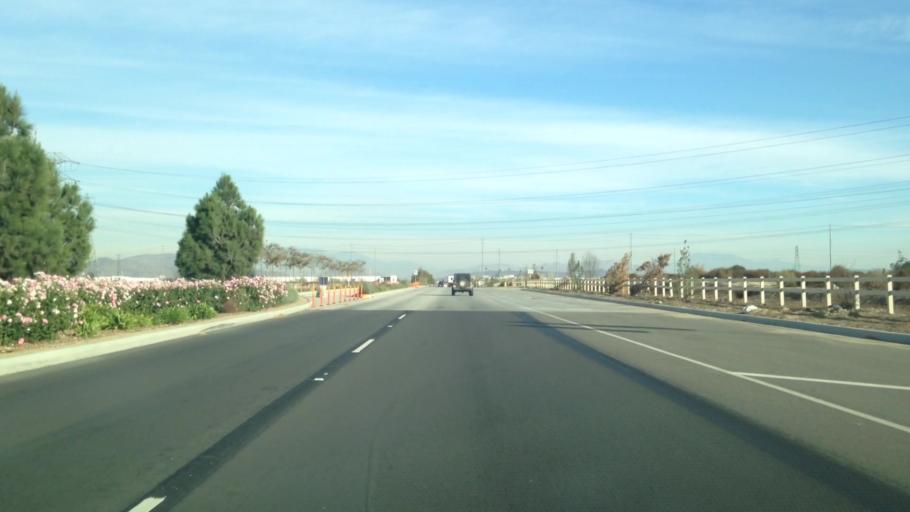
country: US
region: California
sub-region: Riverside County
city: Mira Loma
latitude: 34.0007
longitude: -117.5731
